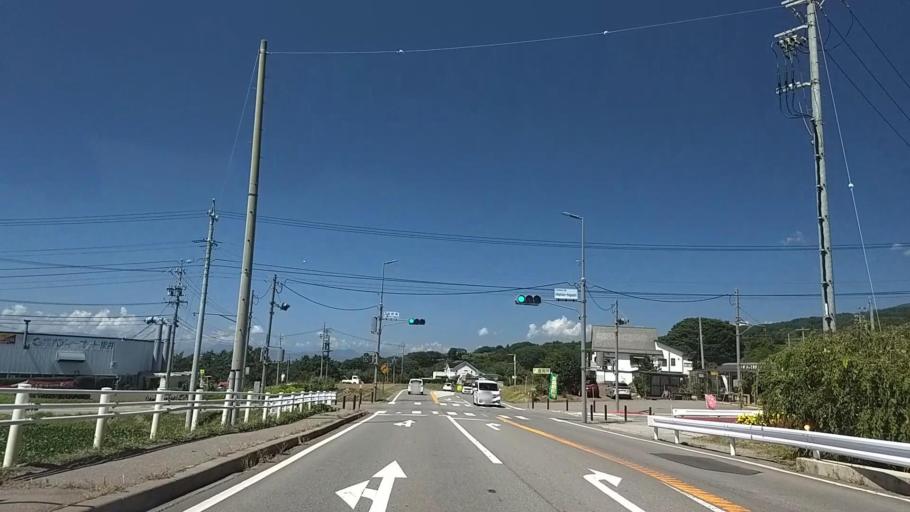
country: JP
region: Nagano
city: Komoro
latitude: 36.3461
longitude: 138.4351
